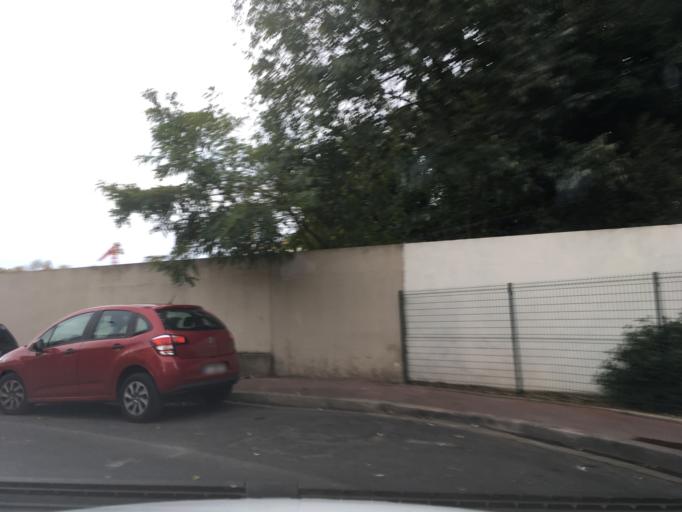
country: FR
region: Languedoc-Roussillon
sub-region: Departement de l'Herault
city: Montpellier
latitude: 43.6210
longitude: 3.8859
